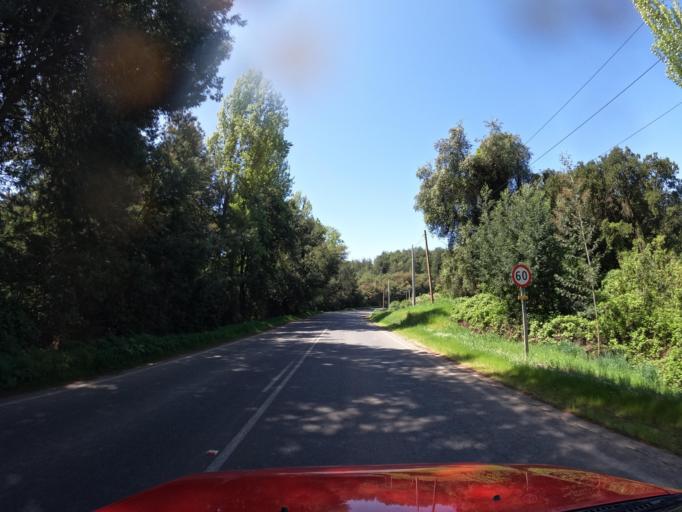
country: CL
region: Maule
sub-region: Provincia de Talca
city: San Clemente
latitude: -35.4868
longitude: -71.2917
